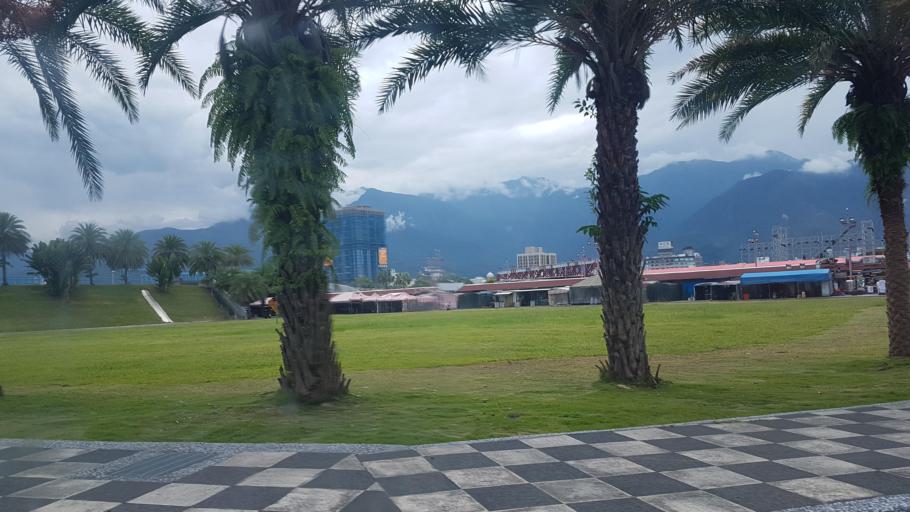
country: TW
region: Taiwan
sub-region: Hualien
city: Hualian
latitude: 23.9716
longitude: 121.6134
